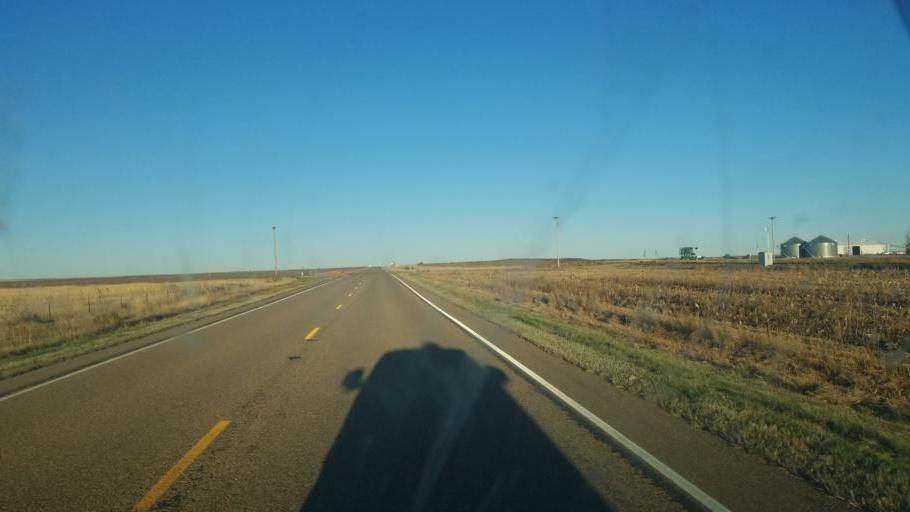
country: US
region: Colorado
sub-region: Cheyenne County
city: Cheyenne Wells
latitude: 38.8108
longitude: -102.4611
